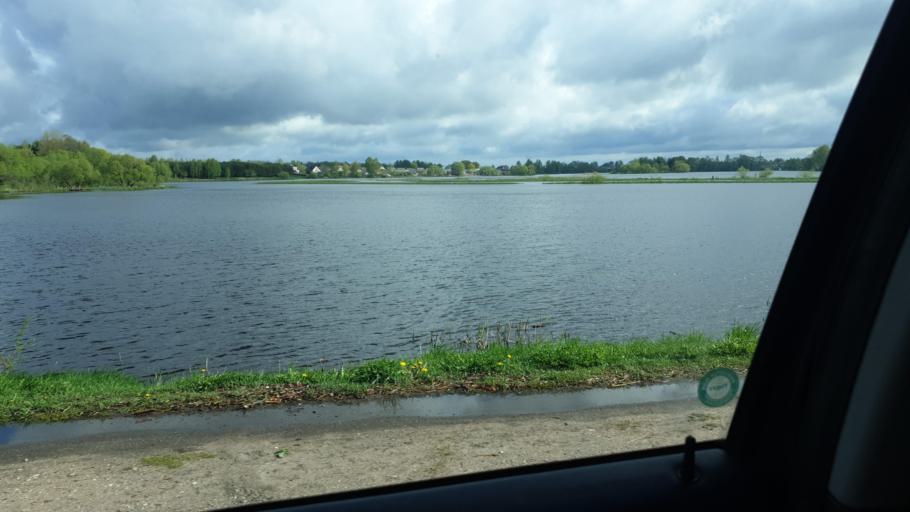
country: BY
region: Vitebsk
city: Lyepyel'
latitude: 54.8771
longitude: 28.6637
